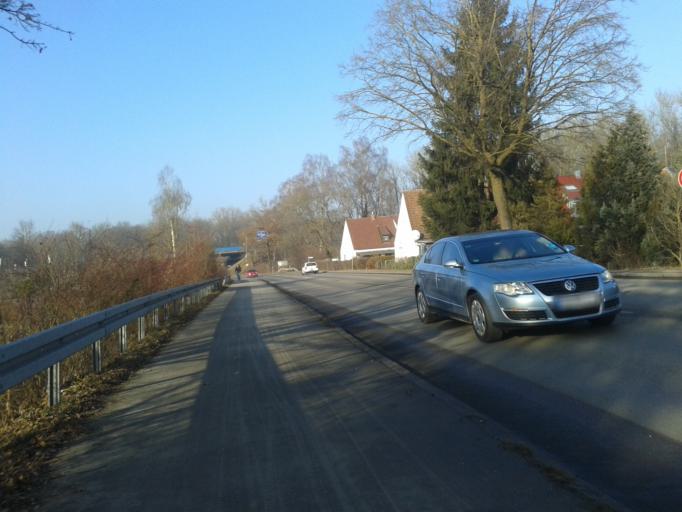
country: DE
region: Baden-Wuerttemberg
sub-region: Tuebingen Region
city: Ulm
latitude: 48.3660
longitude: 9.9909
